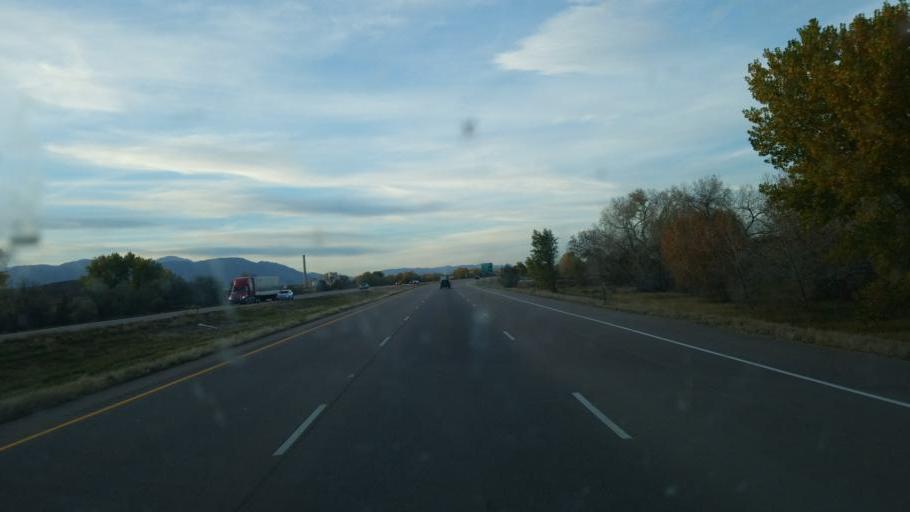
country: US
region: Colorado
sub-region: El Paso County
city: Fountain
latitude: 38.6132
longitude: -104.6852
